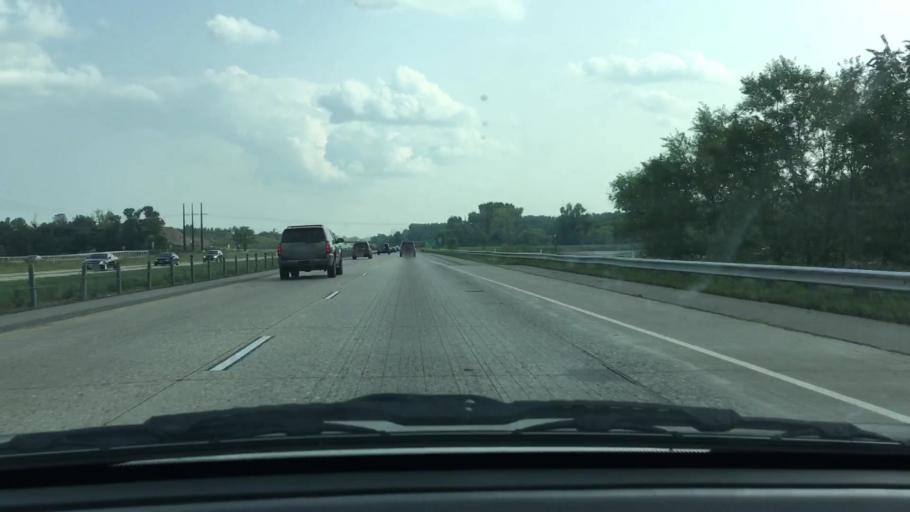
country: US
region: Minnesota
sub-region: Dakota County
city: Lakeville
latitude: 44.6749
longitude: -93.2944
